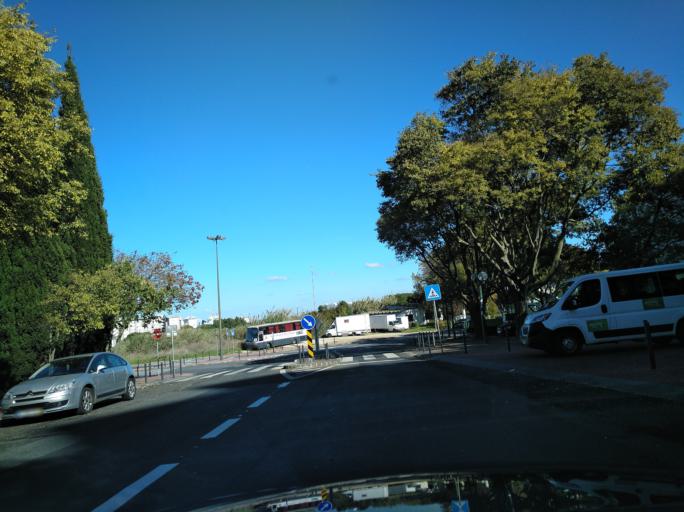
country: PT
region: Lisbon
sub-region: Loures
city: Moscavide
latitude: 38.7474
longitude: -9.1127
